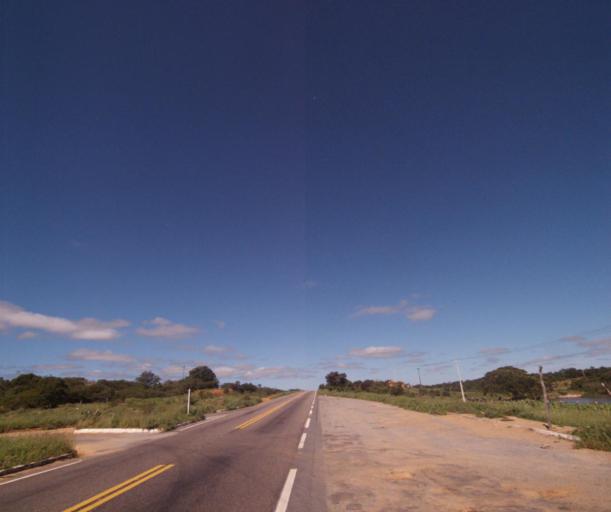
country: BR
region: Bahia
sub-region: Guanambi
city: Guanambi
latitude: -14.2326
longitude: -42.9543
